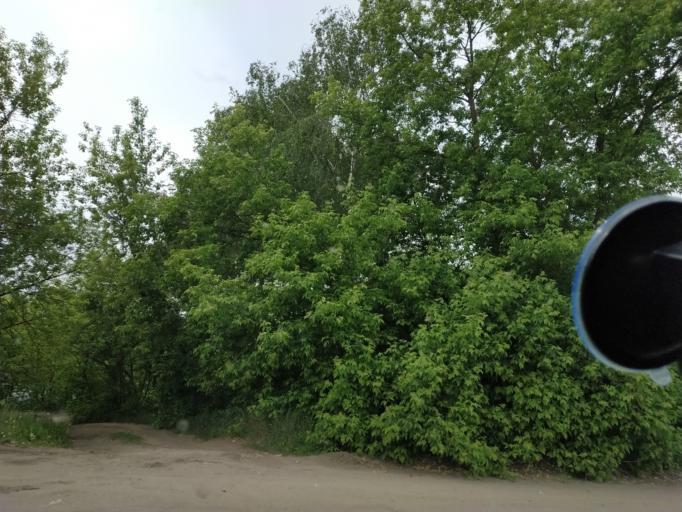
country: RU
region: Moskovskaya
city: Zhukovskiy
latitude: 55.5684
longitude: 38.1155
